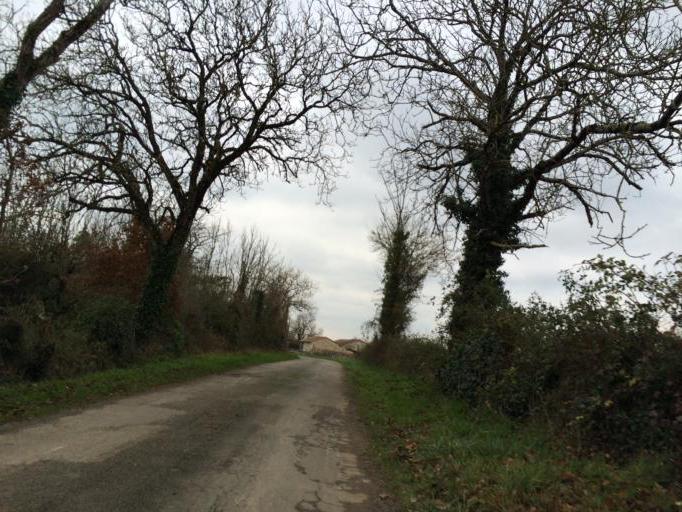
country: FR
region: Poitou-Charentes
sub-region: Departement des Deux-Sevres
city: Sauze-Vaussais
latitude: 46.1578
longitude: 0.1511
